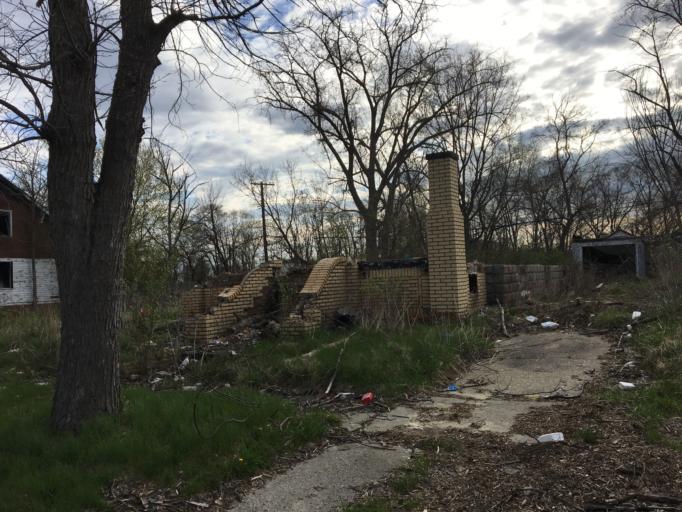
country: US
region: Michigan
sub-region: Oakland County
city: Hazel Park
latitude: 42.4352
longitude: -83.1052
